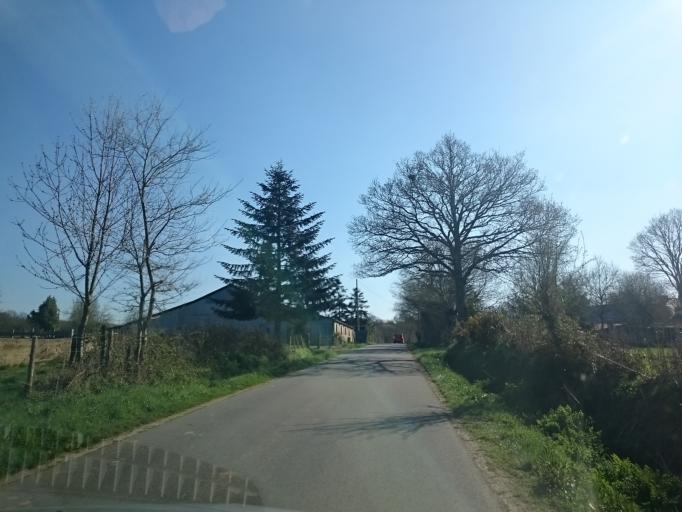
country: FR
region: Brittany
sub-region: Departement d'Ille-et-Vilaine
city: Orgeres
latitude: 47.9775
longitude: -1.6745
